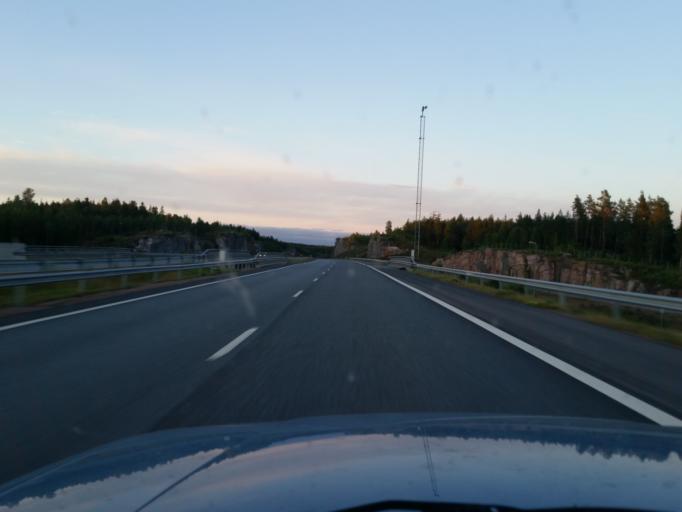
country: FI
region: Varsinais-Suomi
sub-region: Salo
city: Suomusjaervi
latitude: 60.3708
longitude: 23.7066
